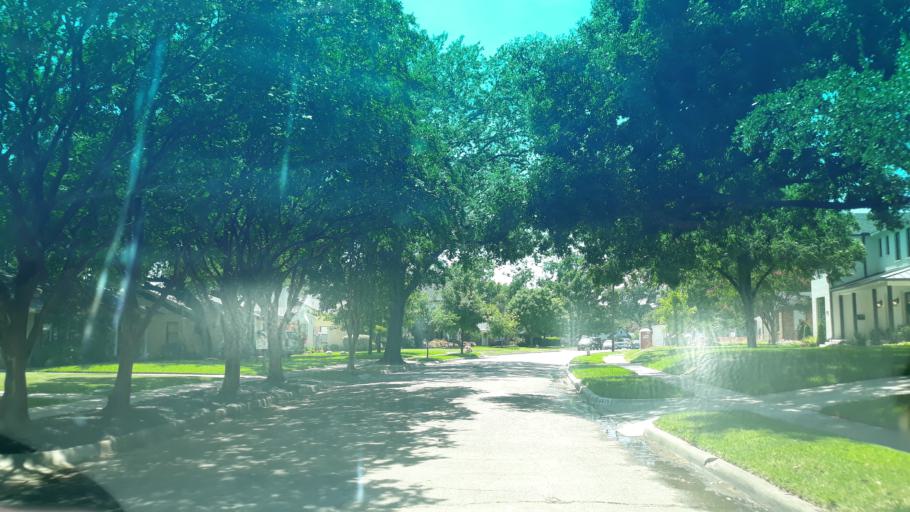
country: US
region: Texas
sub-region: Dallas County
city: Highland Park
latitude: 32.8294
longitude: -96.7429
